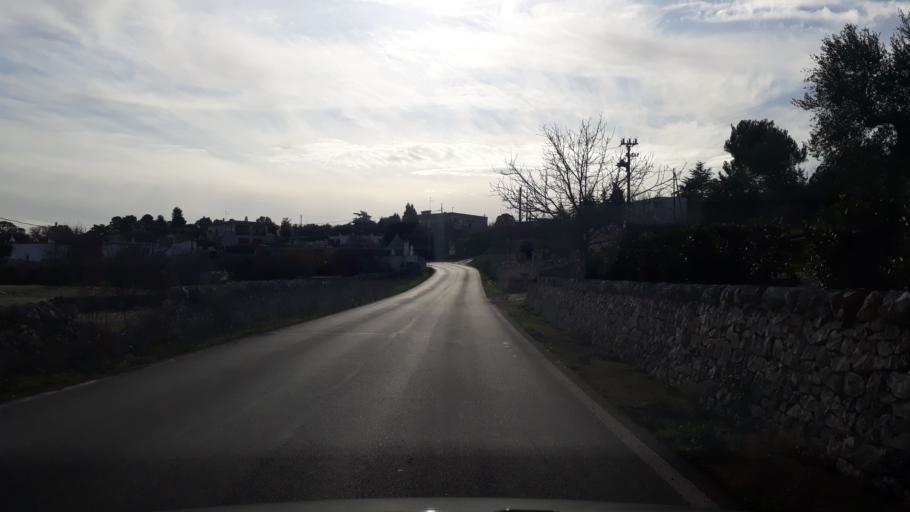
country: IT
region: Apulia
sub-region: Provincia di Taranto
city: Martina Franca
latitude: 40.6797
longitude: 17.3561
